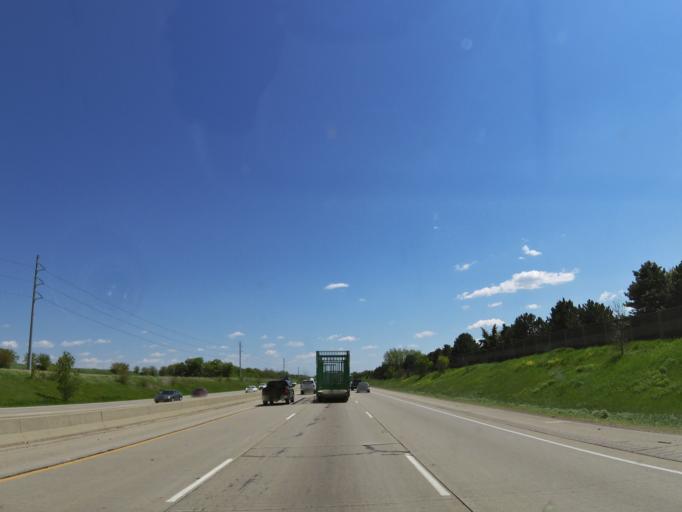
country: US
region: Wisconsin
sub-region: Dane County
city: Monona
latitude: 43.0729
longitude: -89.2801
